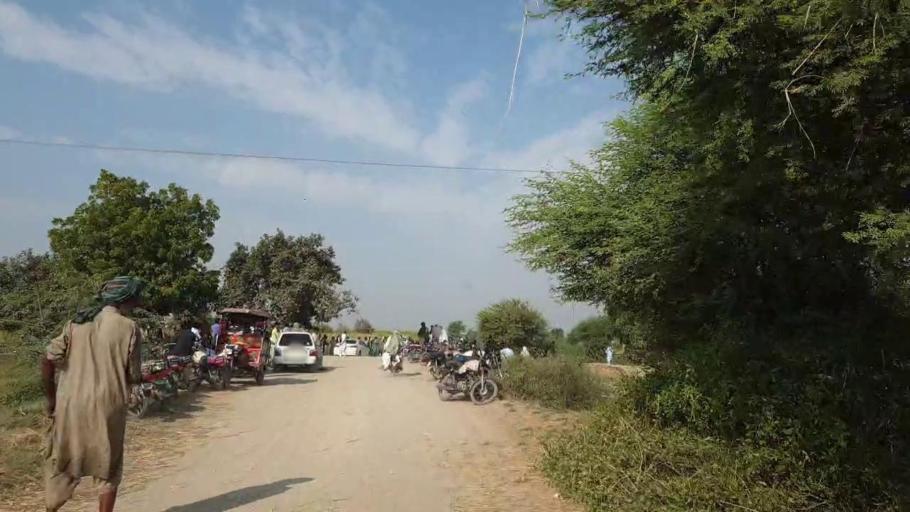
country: PK
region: Sindh
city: Tando Muhammad Khan
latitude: 25.0610
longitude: 68.4146
